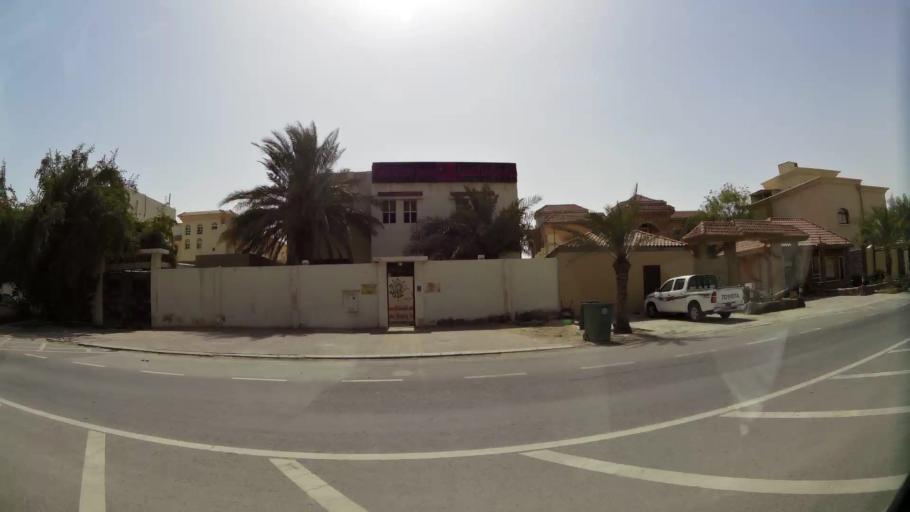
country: QA
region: Baladiyat Umm Salal
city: Umm Salal Muhammad
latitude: 25.3918
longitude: 51.4294
